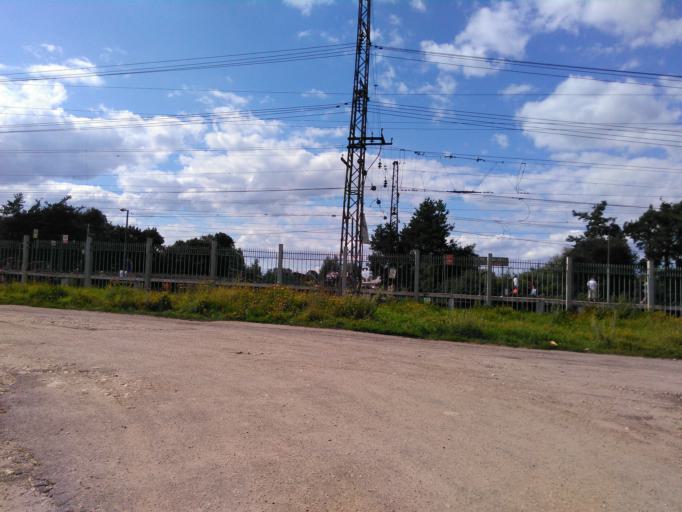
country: RU
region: Vladimir
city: Pokrov
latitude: 55.8682
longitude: 39.1030
